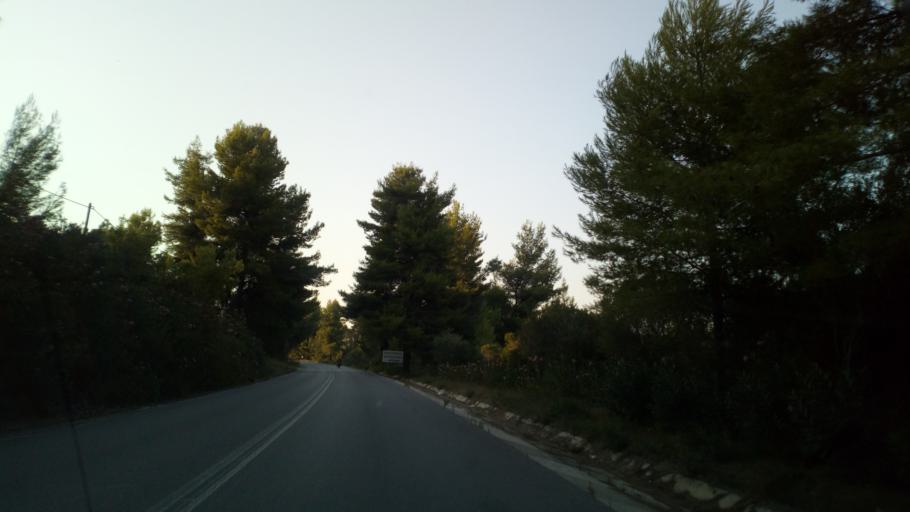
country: GR
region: Central Macedonia
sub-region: Nomos Chalkidikis
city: Pefkochori
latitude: 39.9659
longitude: 23.6727
